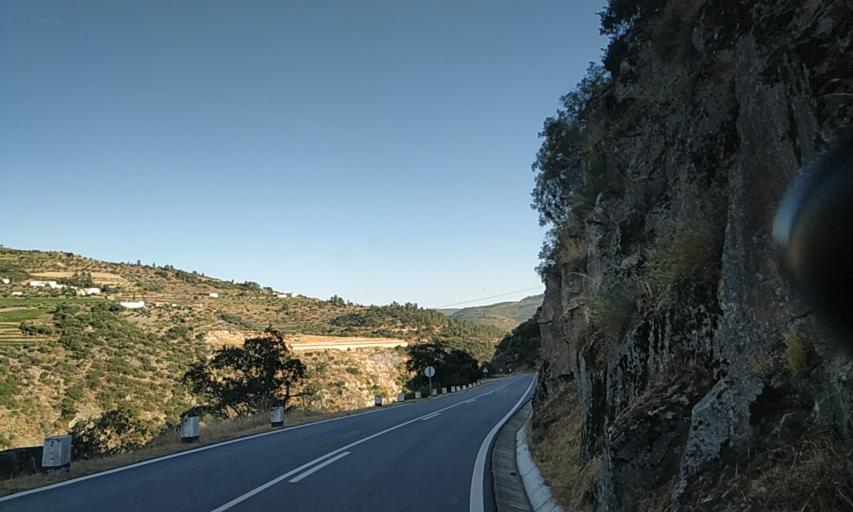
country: PT
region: Viseu
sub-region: Sao Joao da Pesqueira
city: Sao Joao da Pesqueira
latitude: 41.2254
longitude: -7.4238
